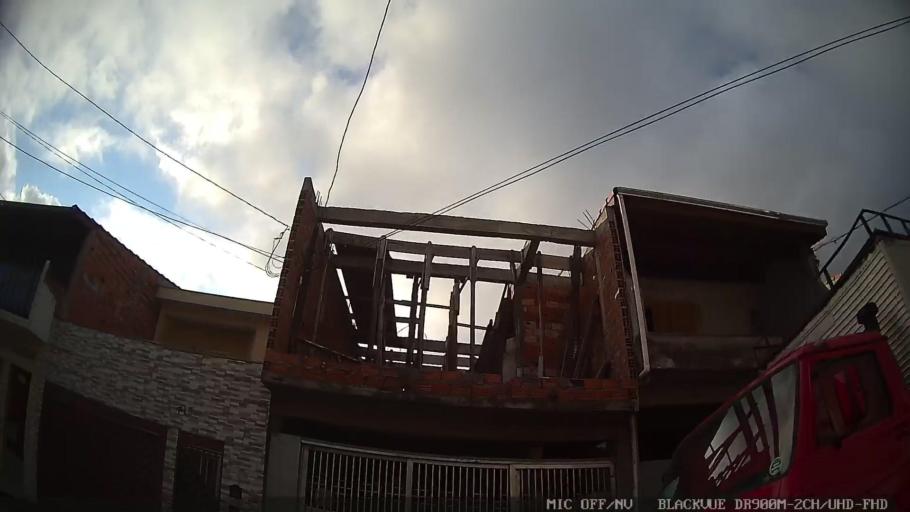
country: BR
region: Sao Paulo
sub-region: Sao Caetano Do Sul
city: Sao Caetano do Sul
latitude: -23.5674
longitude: -46.4848
